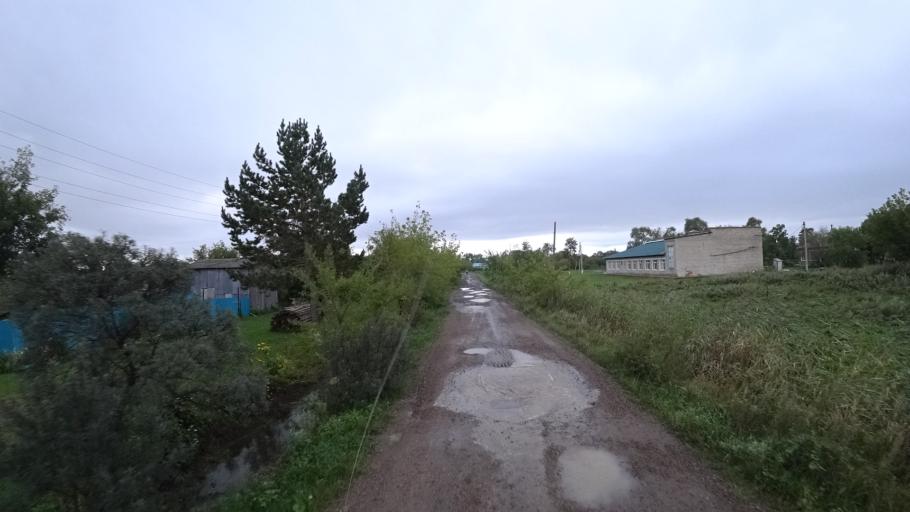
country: RU
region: Primorskiy
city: Chernigovka
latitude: 44.4061
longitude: 132.5320
